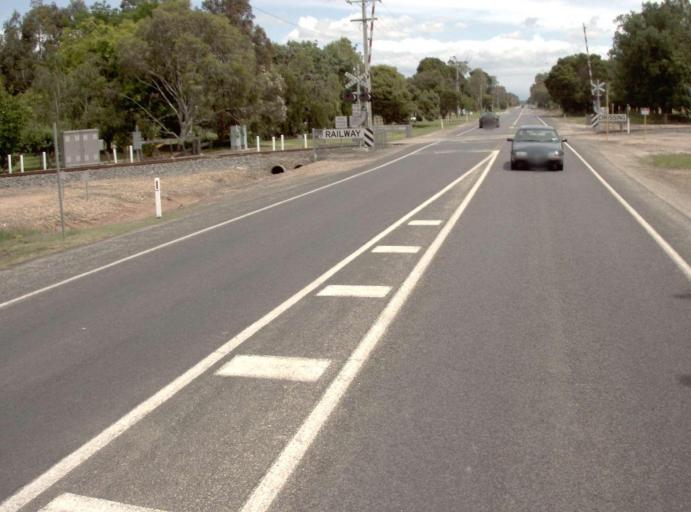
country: AU
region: Victoria
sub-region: Wellington
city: Sale
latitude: -38.0887
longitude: 147.0623
